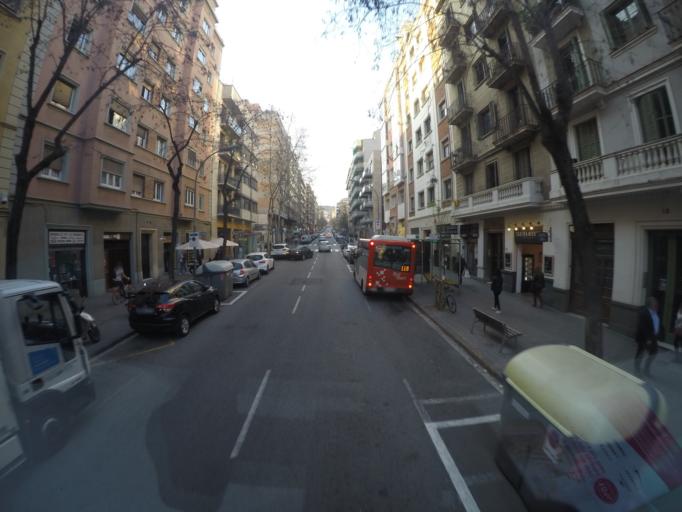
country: ES
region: Catalonia
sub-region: Provincia de Barcelona
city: Gracia
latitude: 41.4062
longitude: 2.1624
